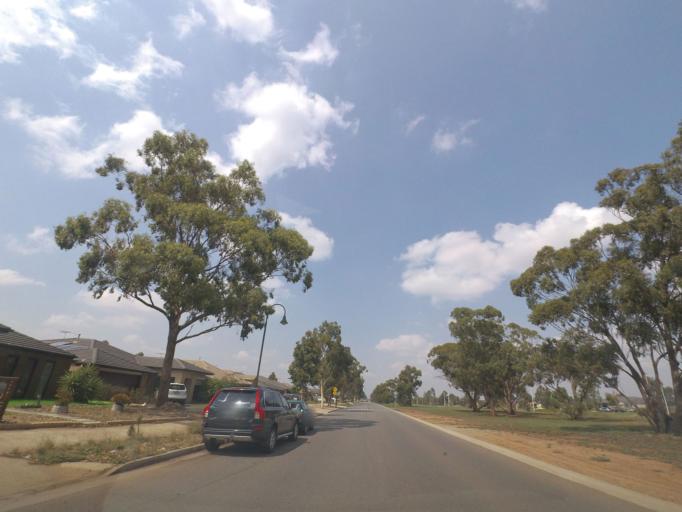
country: AU
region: Victoria
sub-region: Melton
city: Brookfield
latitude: -37.6932
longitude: 144.5480
